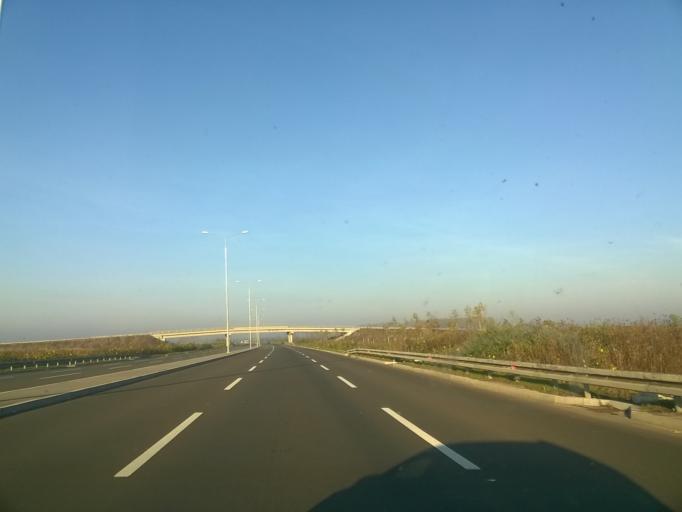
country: RS
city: Ovca
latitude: 44.9133
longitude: 20.5005
